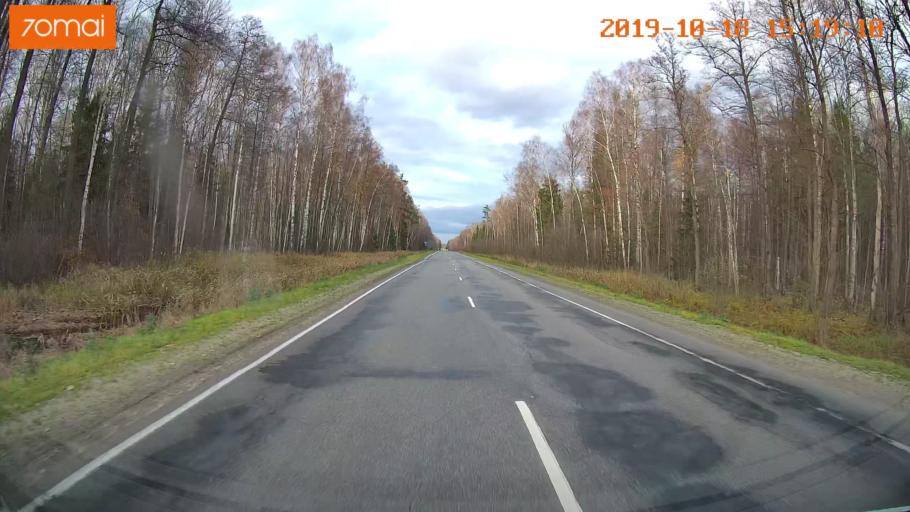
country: RU
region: Vladimir
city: Anopino
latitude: 55.6690
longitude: 40.7355
